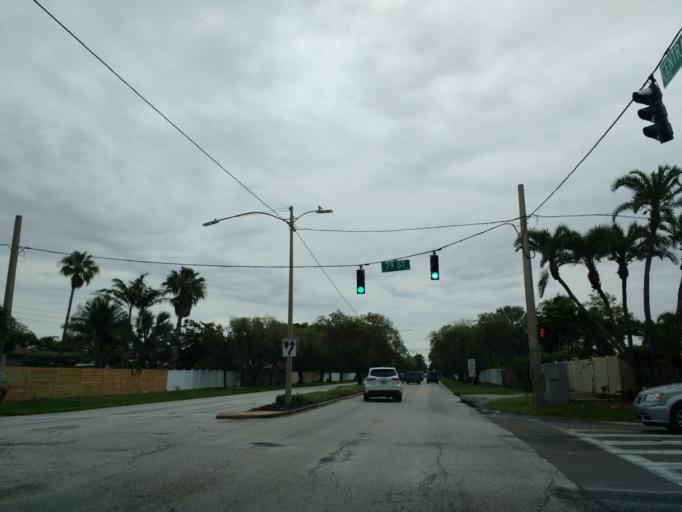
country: US
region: Florida
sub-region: Pinellas County
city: South Pasadena
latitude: 27.7707
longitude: -82.7473
